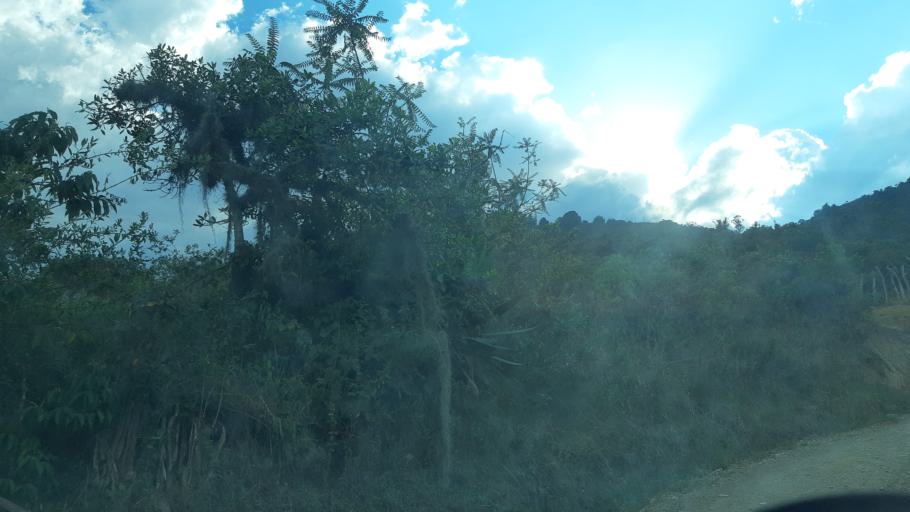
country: CO
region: Boyaca
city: Santa Sofia
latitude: 5.7418
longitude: -73.5783
